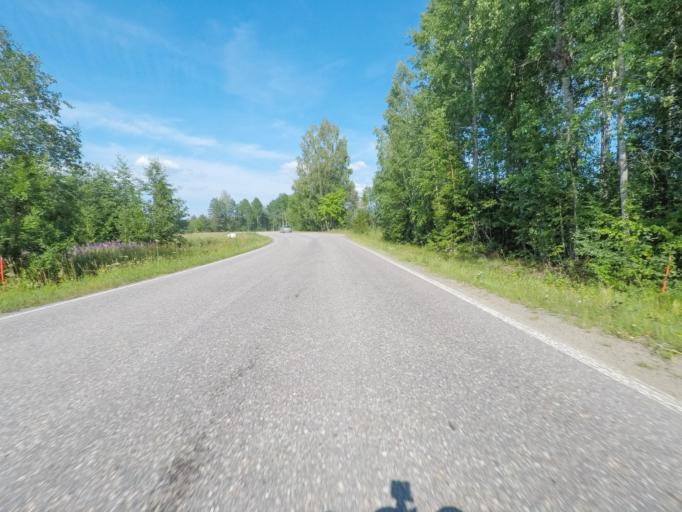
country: FI
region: Southern Savonia
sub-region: Mikkeli
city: Puumala
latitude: 61.5781
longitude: 28.1879
